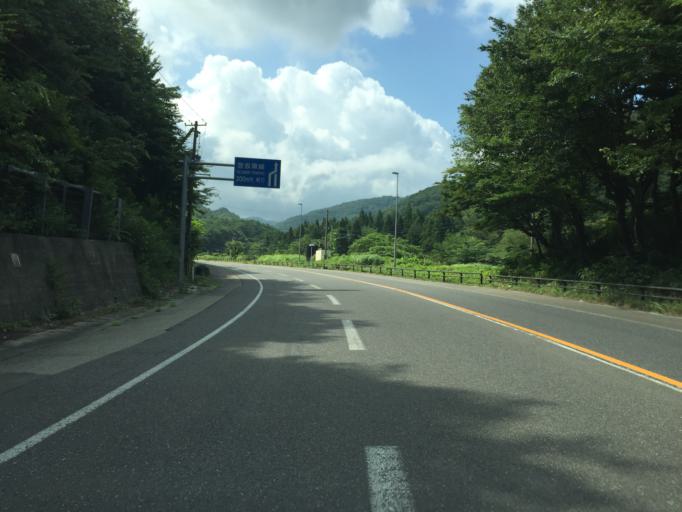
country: JP
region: Fukushima
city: Inawashiro
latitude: 37.4866
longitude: 140.2011
